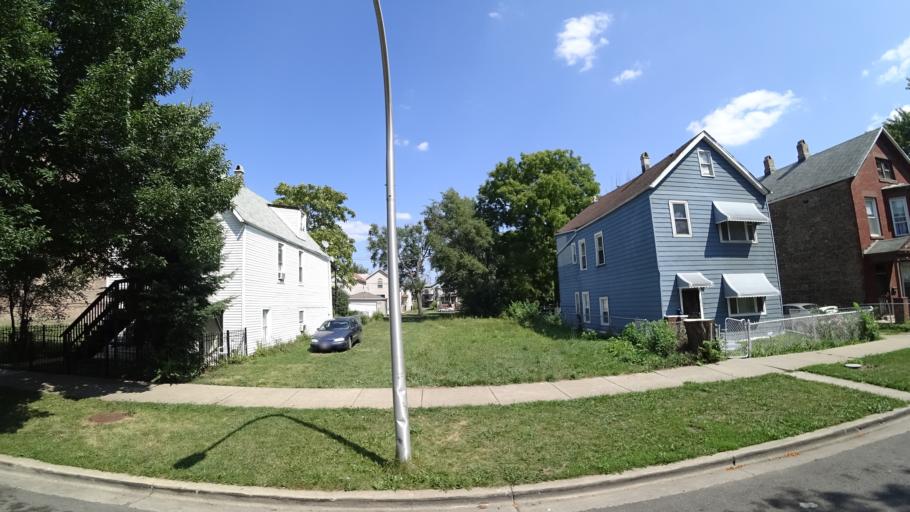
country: US
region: Illinois
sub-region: Cook County
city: Cicero
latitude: 41.8596
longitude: -87.7299
